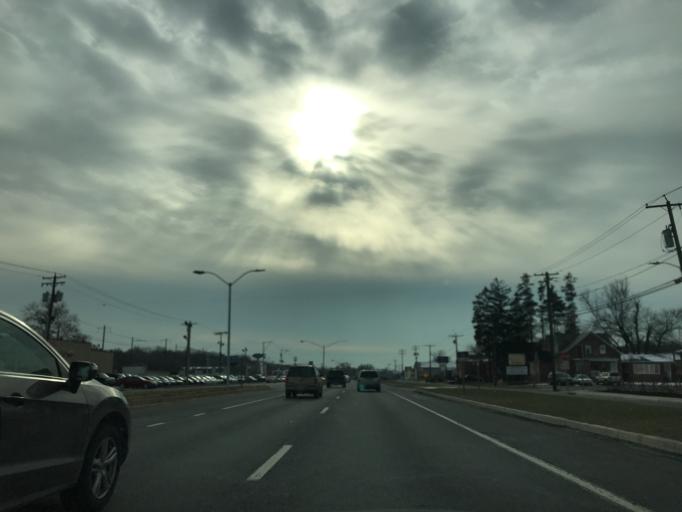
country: US
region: Maryland
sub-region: Harford County
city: Aberdeen
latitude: 39.5045
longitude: -76.1667
